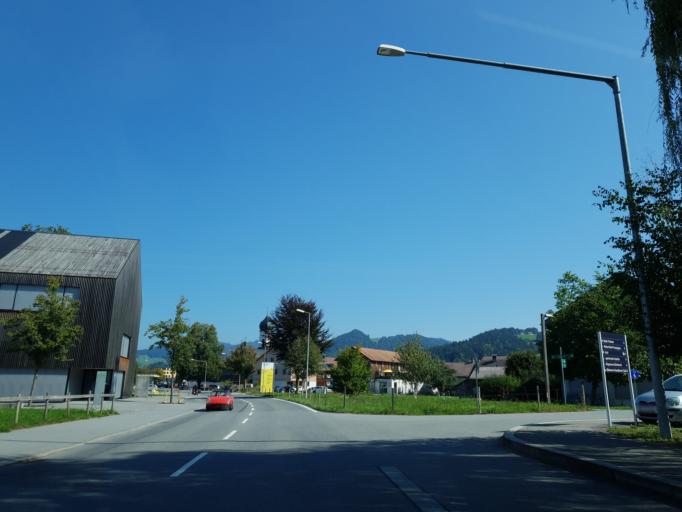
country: AT
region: Vorarlberg
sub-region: Politischer Bezirk Bregenz
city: Andelsbuch
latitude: 47.4119
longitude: 9.8938
